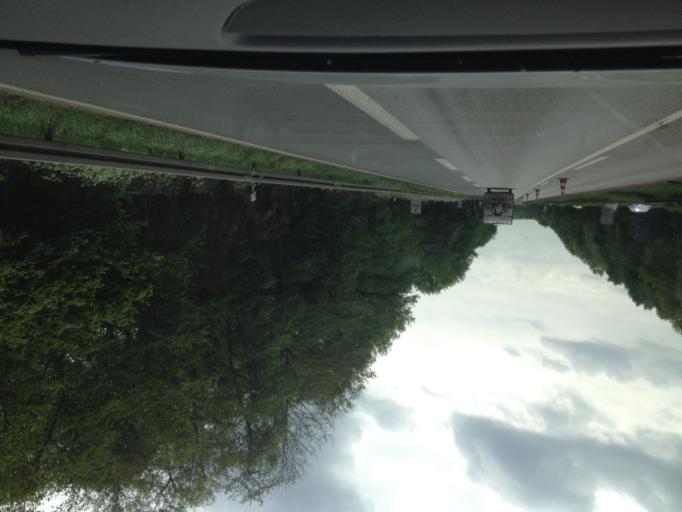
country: DE
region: North Rhine-Westphalia
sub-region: Regierungsbezirk Dusseldorf
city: Dinslaken
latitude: 51.5848
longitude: 6.7876
